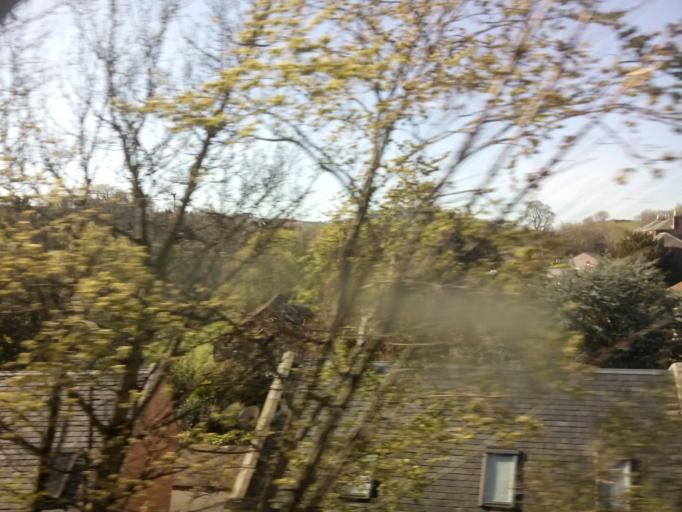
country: GB
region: Scotland
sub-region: East Lothian
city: East Linton
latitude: 55.9848
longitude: -2.6552
